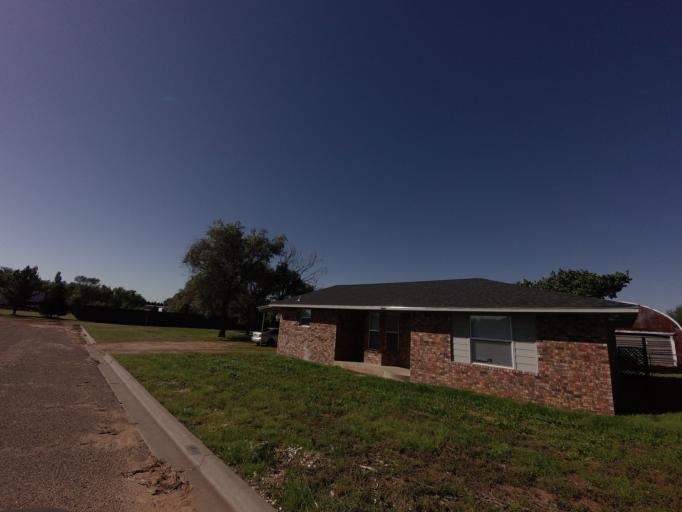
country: US
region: New Mexico
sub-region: Curry County
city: Clovis
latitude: 34.4314
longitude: -103.1929
